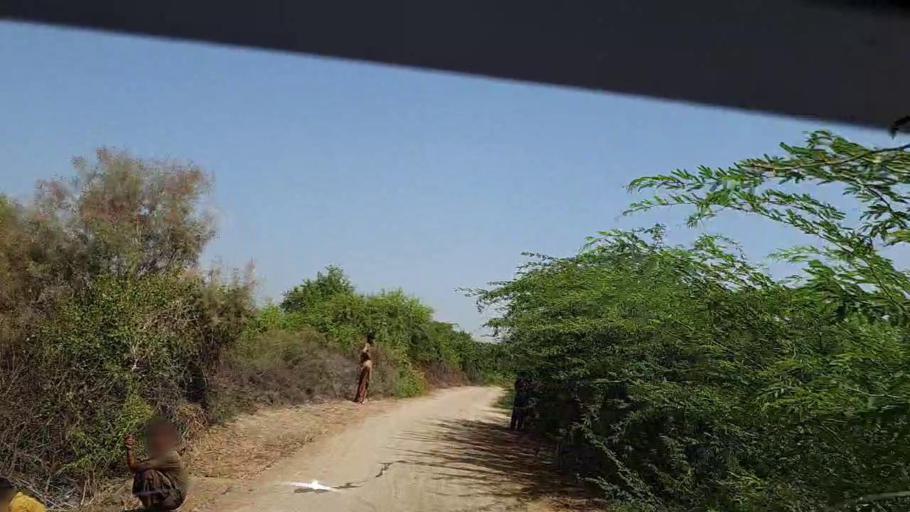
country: PK
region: Sindh
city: Rajo Khanani
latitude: 24.9354
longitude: 68.8813
